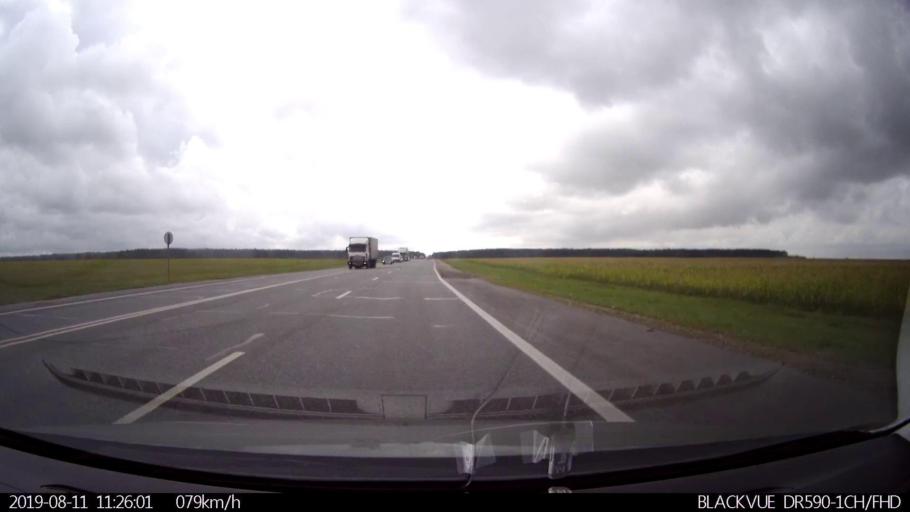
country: RU
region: Ulyanovsk
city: Krasnyy Gulyay
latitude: 54.1106
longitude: 48.2365
